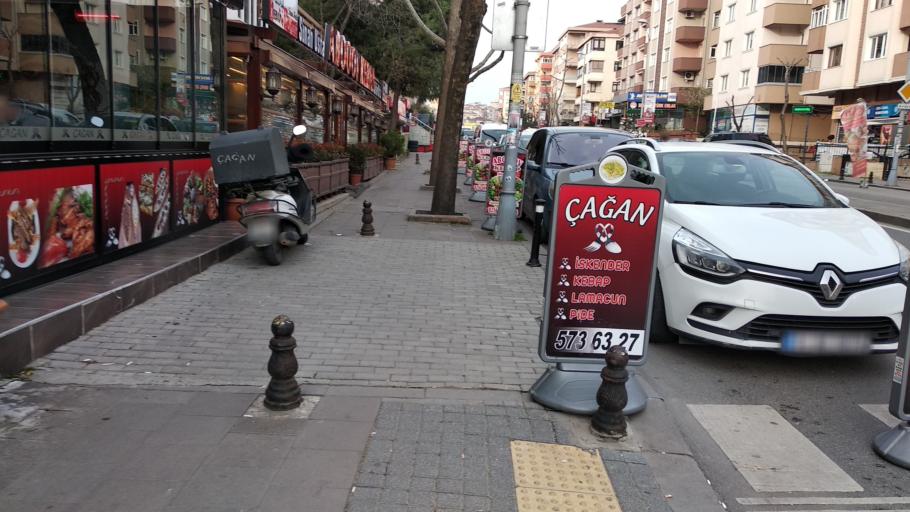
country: TR
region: Istanbul
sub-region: Atasehir
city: Atasehir
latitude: 40.9697
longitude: 29.1165
